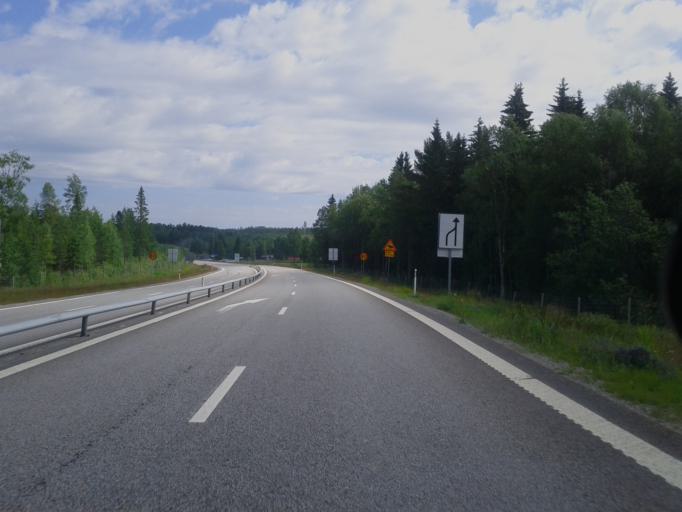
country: SE
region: Vaesternorrland
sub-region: OErnskoeldsviks Kommun
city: Ornskoldsvik
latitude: 63.2958
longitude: 18.8804
